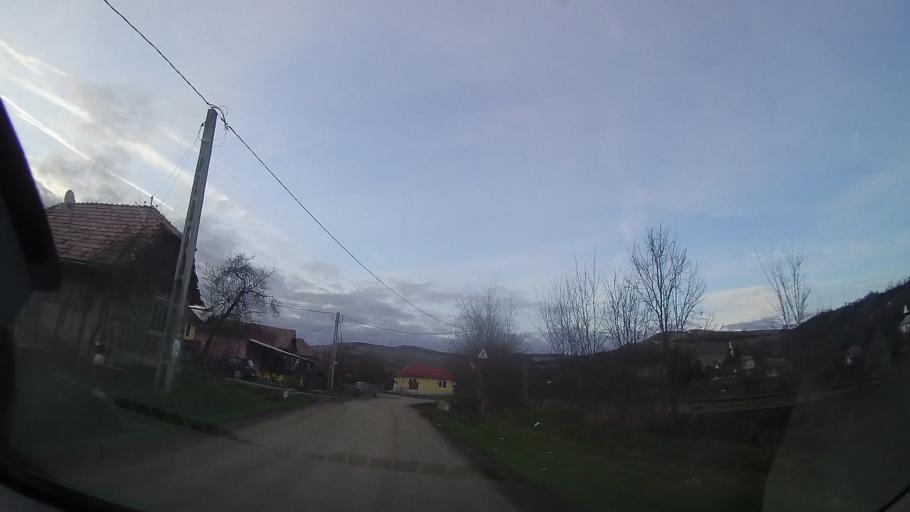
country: RO
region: Cluj
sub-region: Comuna Geaca
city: Geaca
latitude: 46.8537
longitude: 24.0480
